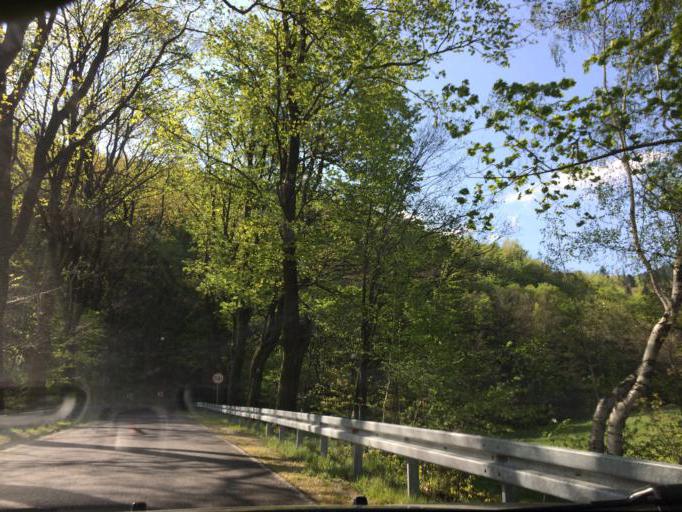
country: PL
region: Lower Silesian Voivodeship
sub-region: Powiat klodzki
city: Jugow
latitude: 50.6656
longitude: 16.5410
